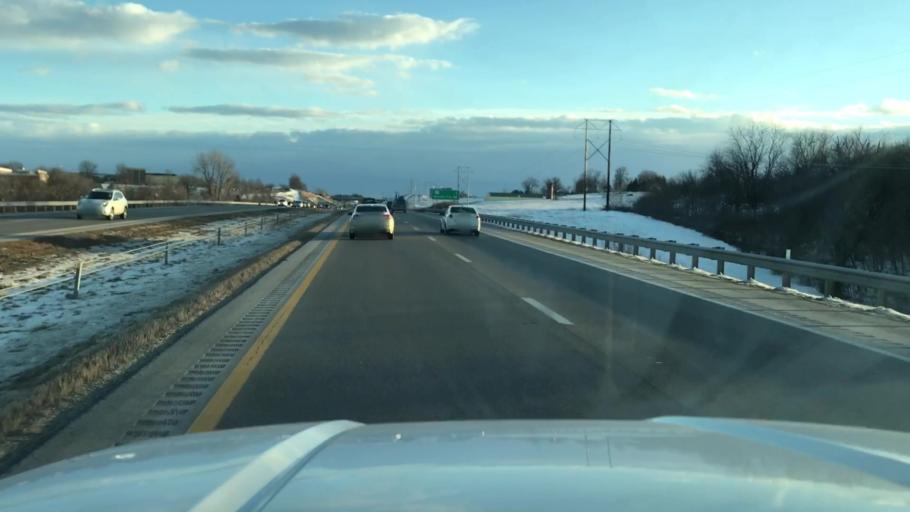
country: US
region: Missouri
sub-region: Buchanan County
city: Saint Joseph
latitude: 39.7647
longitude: -94.7920
